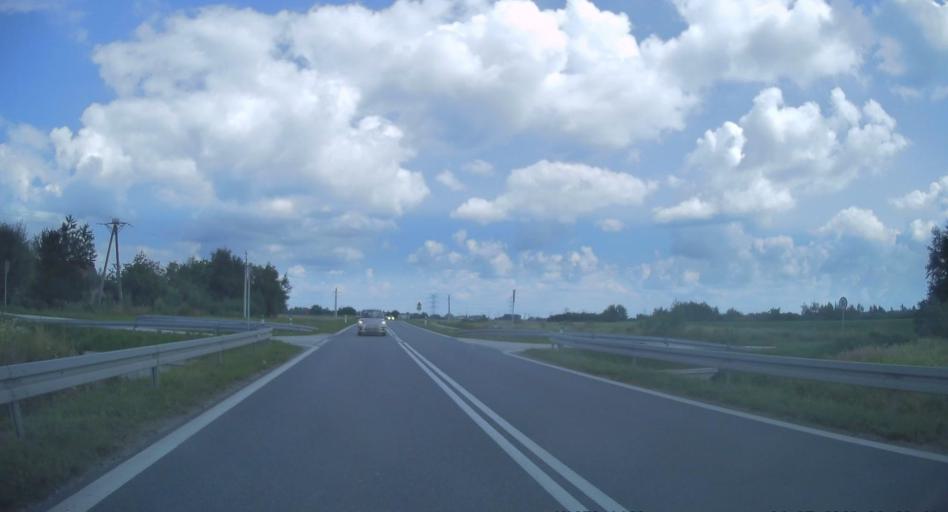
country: PL
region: Lesser Poland Voivodeship
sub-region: Powiat tarnowski
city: Wielka Wies
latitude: 49.9359
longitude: 20.8452
